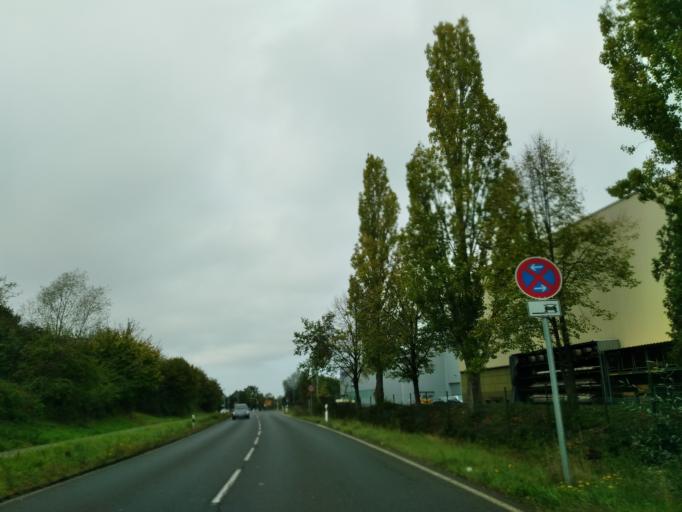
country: DE
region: North Rhine-Westphalia
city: Sankt Augustin
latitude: 50.7509
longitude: 7.1594
